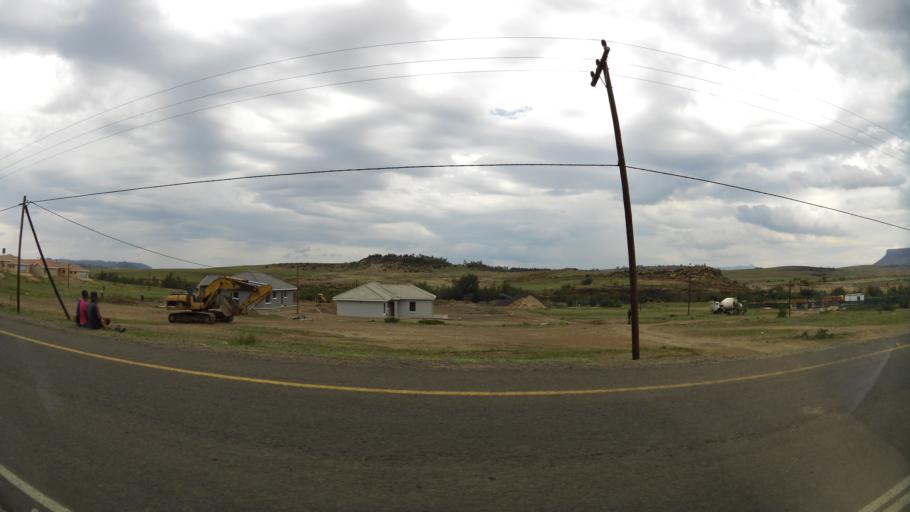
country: LS
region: Maseru
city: Maseru
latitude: -29.3967
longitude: 27.4747
